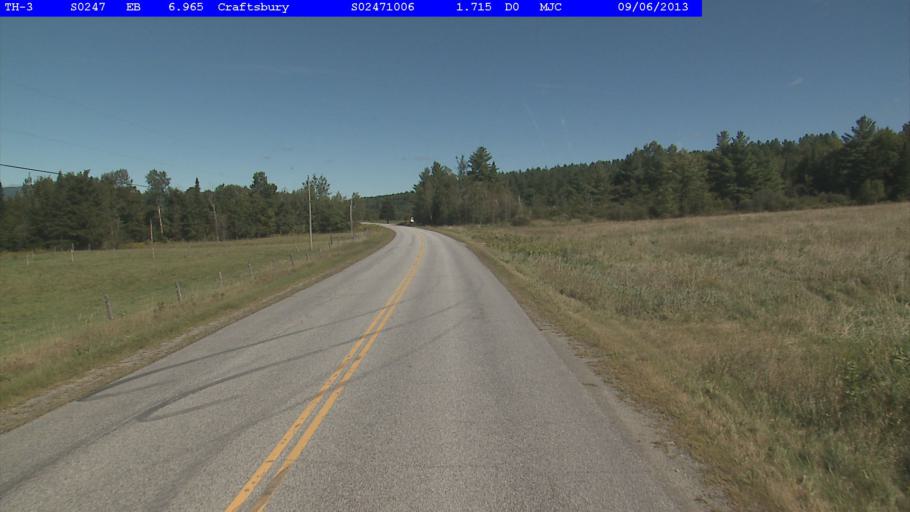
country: US
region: Vermont
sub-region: Caledonia County
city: Hardwick
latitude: 44.6362
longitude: -72.4202
